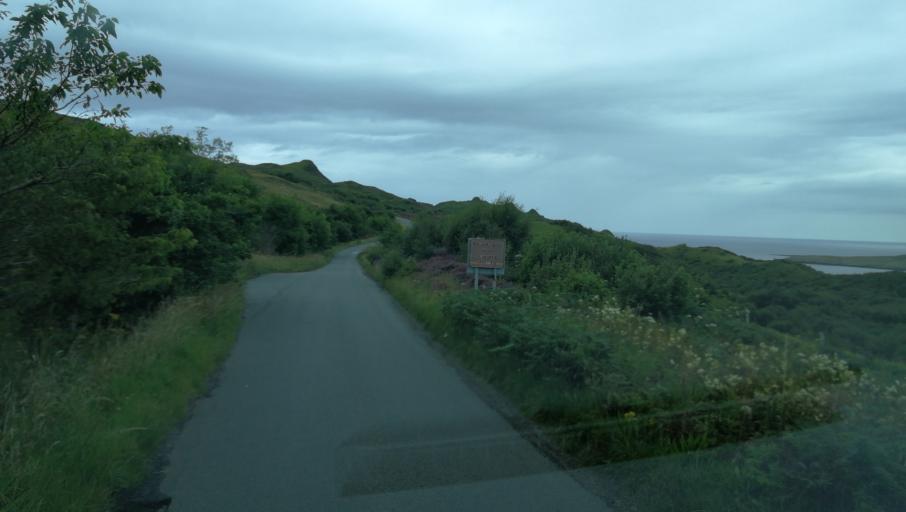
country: GB
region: Scotland
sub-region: Highland
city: Portree
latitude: 57.6451
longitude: -6.2424
